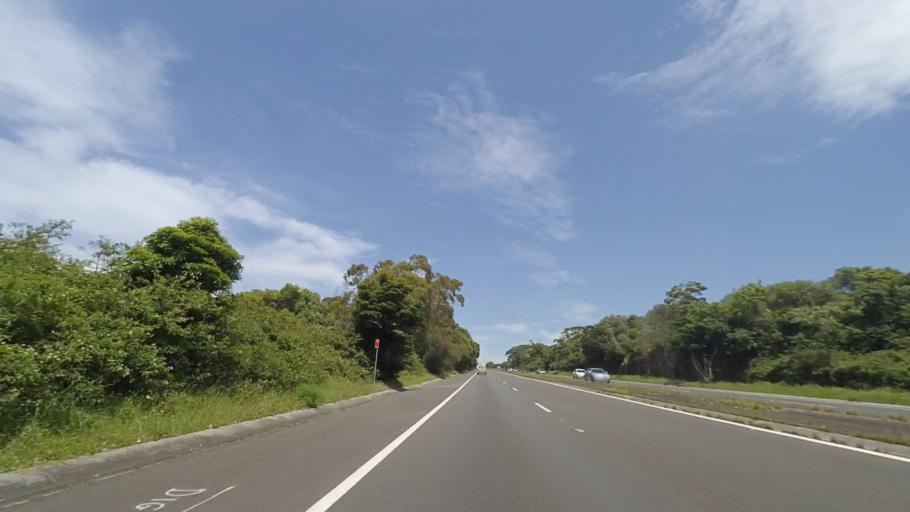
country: AU
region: New South Wales
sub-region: Kiama
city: Kiama
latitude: -34.6687
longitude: 150.8447
